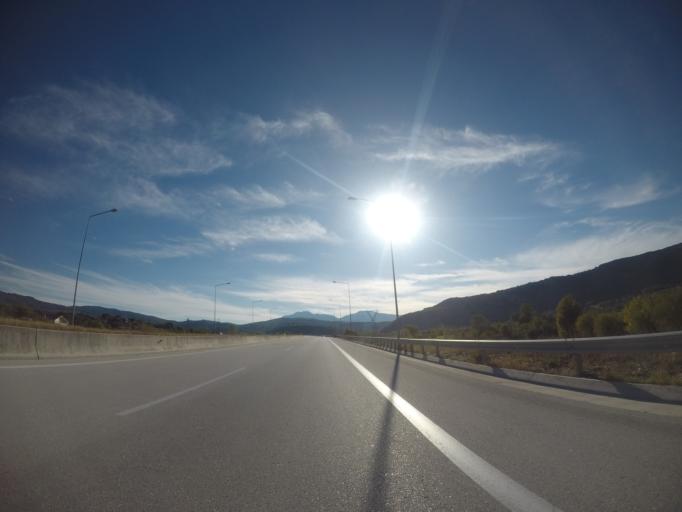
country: GR
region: Epirus
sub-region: Nomos Ioanninon
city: Koutselio
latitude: 39.6086
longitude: 20.9378
